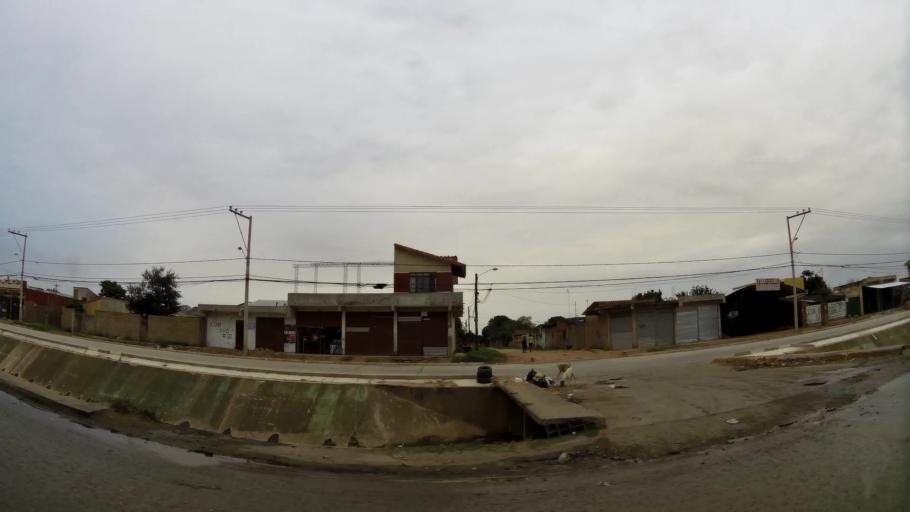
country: BO
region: Santa Cruz
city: Santa Cruz de la Sierra
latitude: -17.8601
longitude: -63.1742
